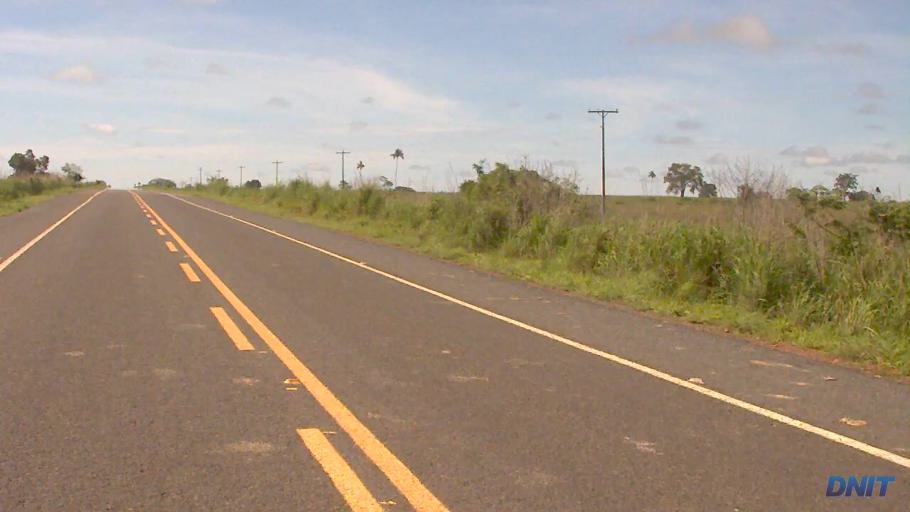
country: BR
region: Goias
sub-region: Sao Miguel Do Araguaia
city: Sao Miguel do Araguaia
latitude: -13.3482
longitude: -50.1501
